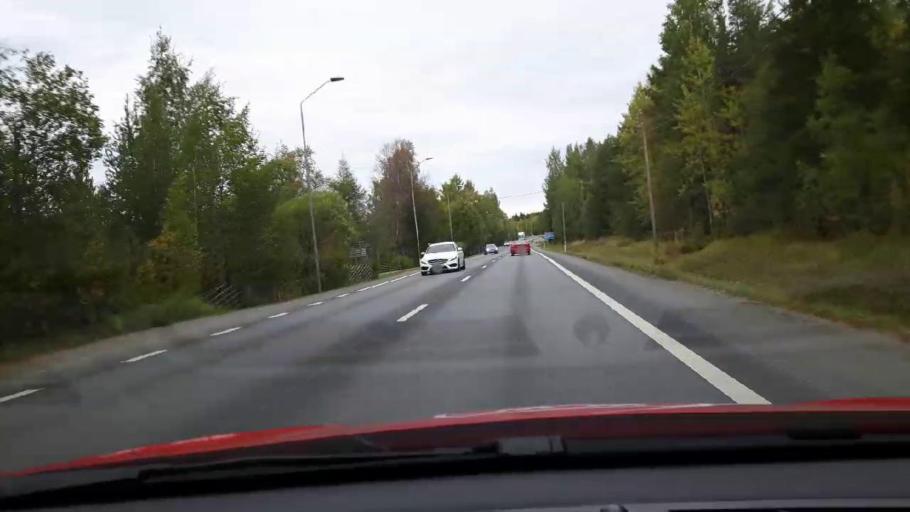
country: SE
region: Jaemtland
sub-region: OEstersunds Kommun
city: Brunflo
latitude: 63.1018
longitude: 14.7962
